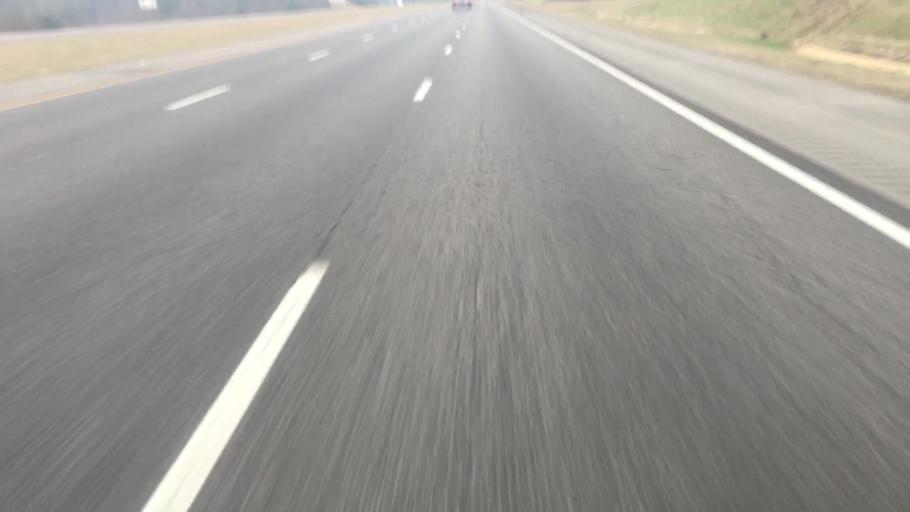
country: US
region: Alabama
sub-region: Jefferson County
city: Adamsville
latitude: 33.6095
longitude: -86.9276
